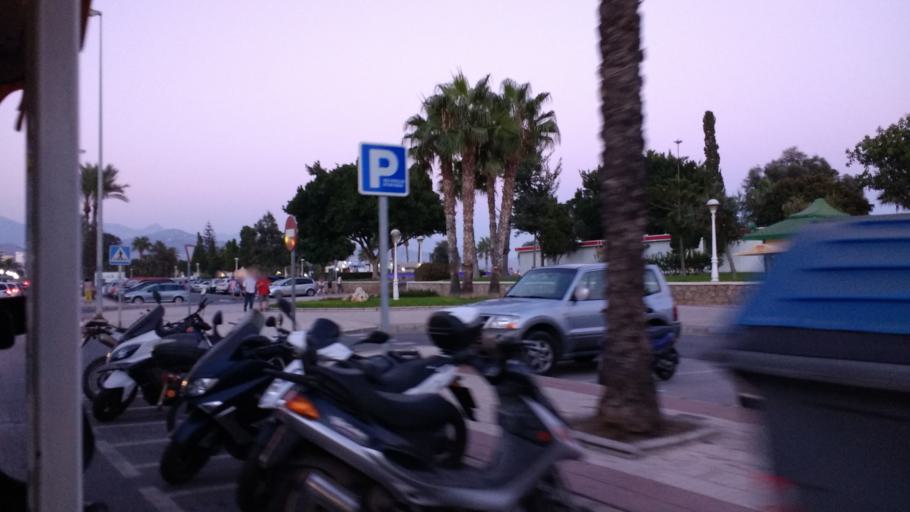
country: ES
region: Andalusia
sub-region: Provincia de Malaga
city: Velez-Malaga
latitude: 36.7378
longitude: -4.0944
